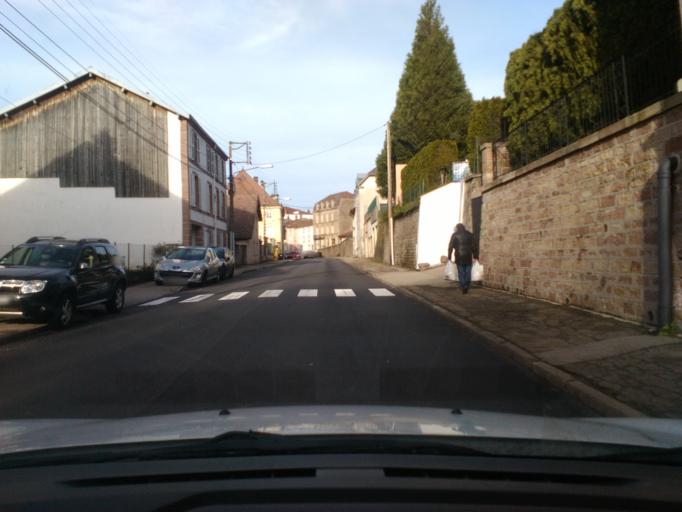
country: FR
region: Lorraine
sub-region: Departement des Vosges
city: Bruyeres
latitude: 48.2067
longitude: 6.7219
